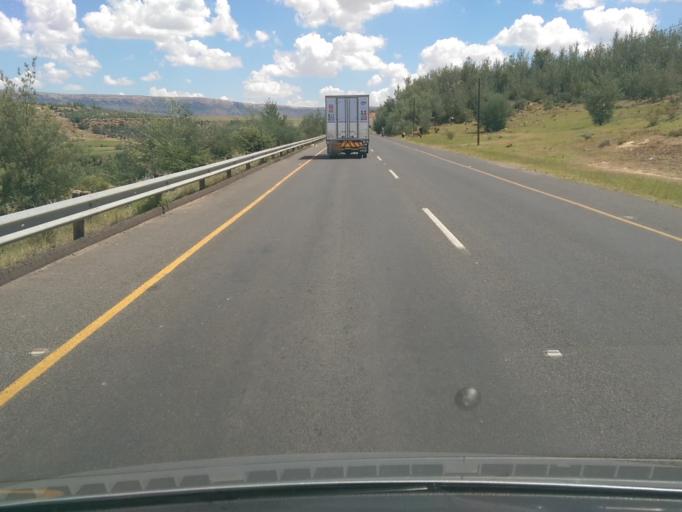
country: LS
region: Maseru
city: Maseru
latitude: -29.3984
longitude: 27.5345
